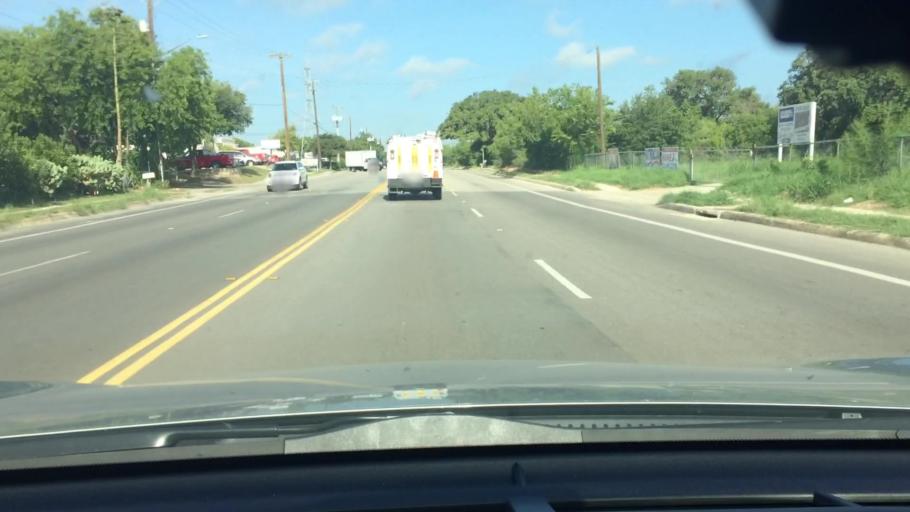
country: US
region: Texas
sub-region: Bexar County
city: China Grove
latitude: 29.3742
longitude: -98.4001
